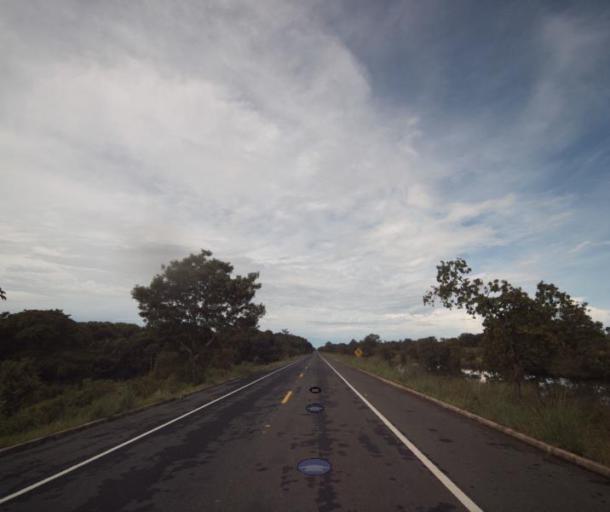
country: BR
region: Goias
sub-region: Sao Miguel Do Araguaia
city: Sao Miguel do Araguaia
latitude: -13.2859
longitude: -50.4795
